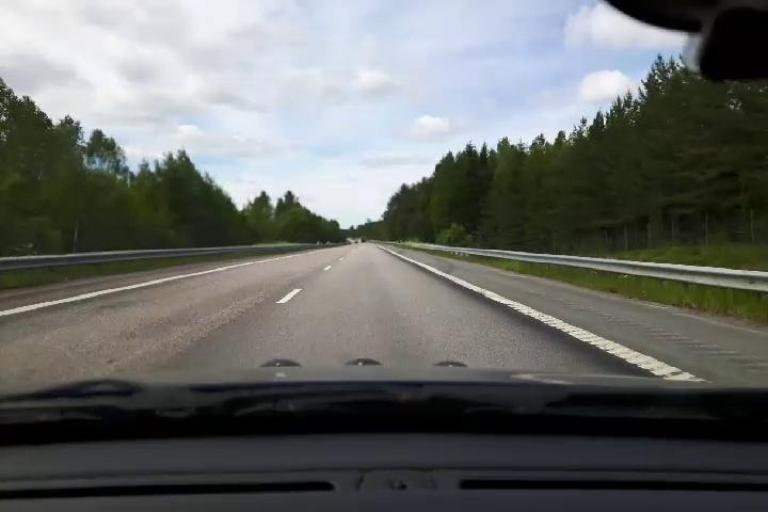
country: SE
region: Uppsala
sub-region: Alvkarleby Kommun
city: AElvkarleby
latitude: 60.4815
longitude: 17.3649
